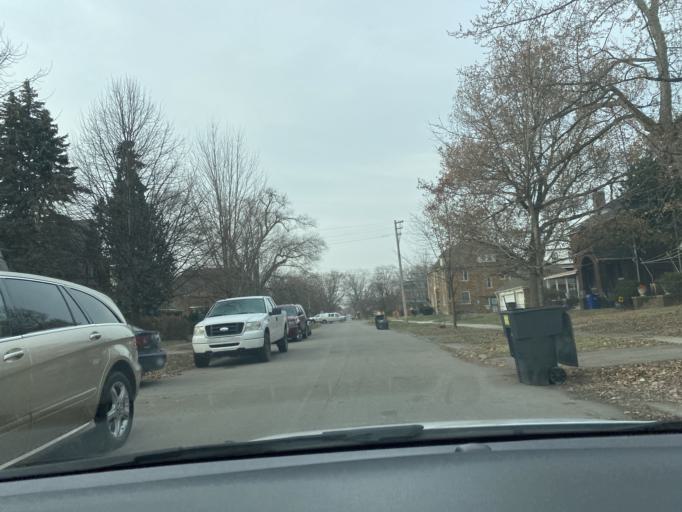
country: US
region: Michigan
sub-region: Wayne County
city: Highland Park
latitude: 42.3817
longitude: -83.1343
